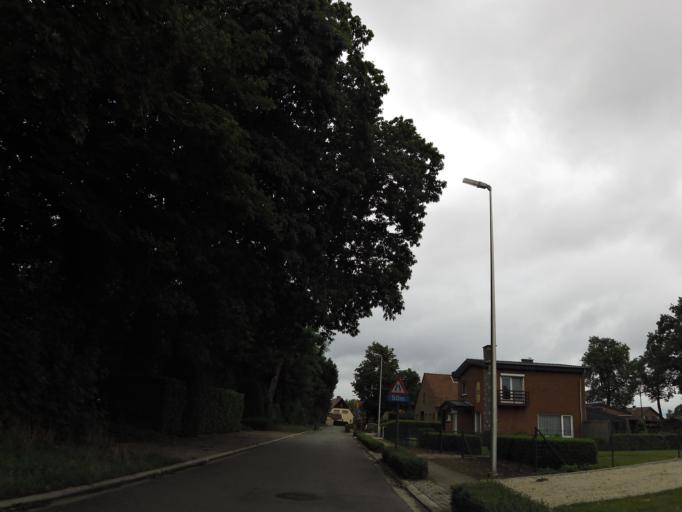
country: BE
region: Flanders
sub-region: Provincie Limburg
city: Bree
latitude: 51.1308
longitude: 5.5913
